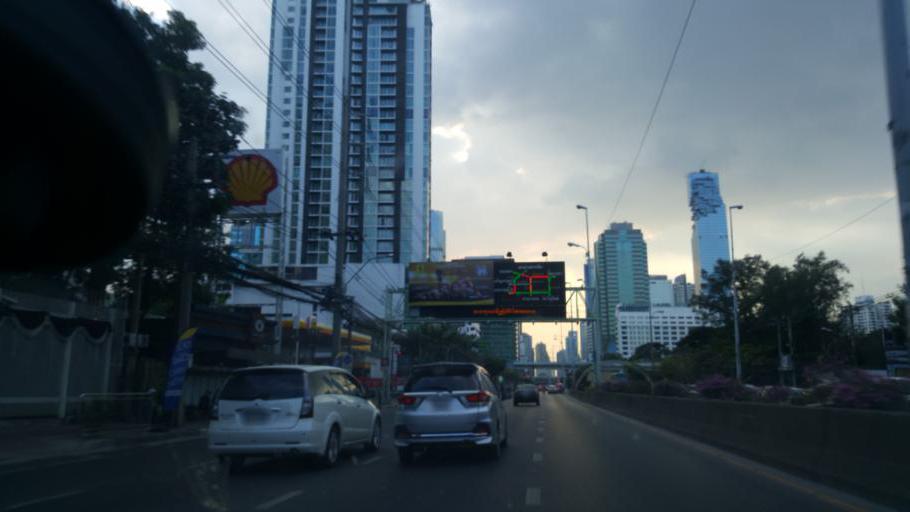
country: TH
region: Bangkok
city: Bang Rak
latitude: 13.7239
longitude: 100.5375
